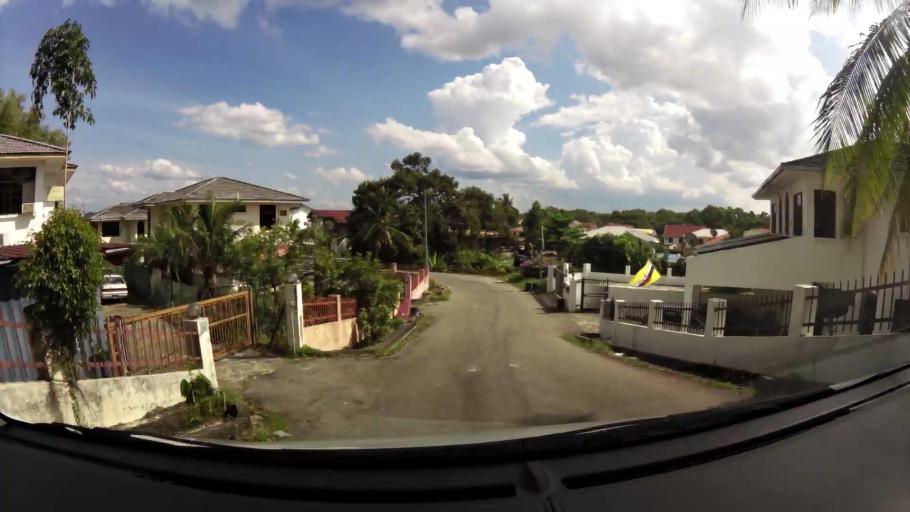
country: BN
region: Brunei and Muara
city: Bandar Seri Begawan
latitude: 4.9561
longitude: 114.9509
